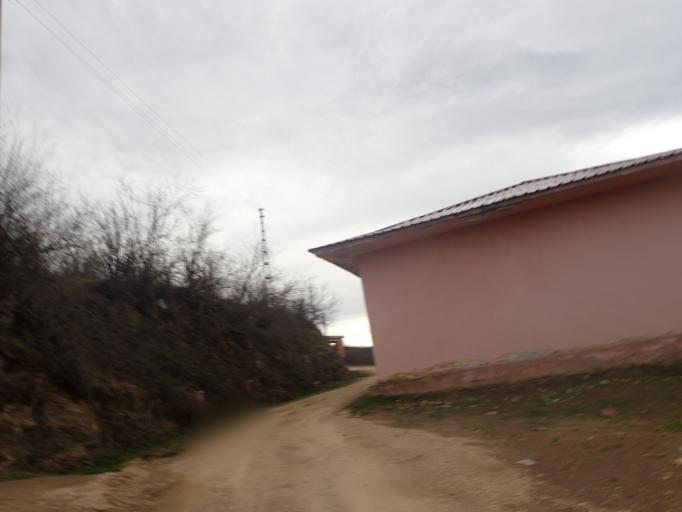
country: TR
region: Ordu
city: Camas
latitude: 40.8874
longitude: 37.5145
